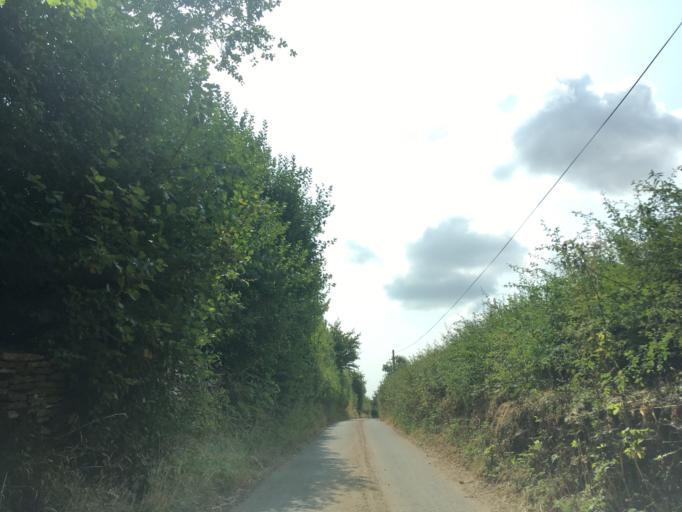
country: GB
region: England
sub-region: Gloucestershire
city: Nailsworth
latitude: 51.6750
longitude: -2.2280
